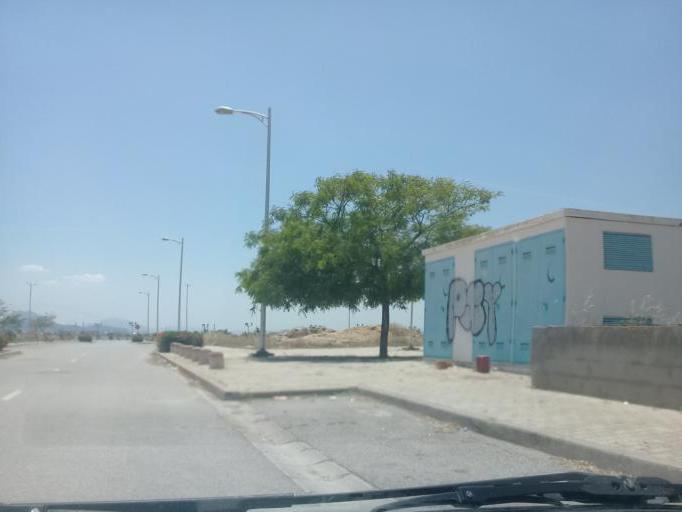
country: TN
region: Tunis
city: La Goulette
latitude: 36.8427
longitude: 10.2807
